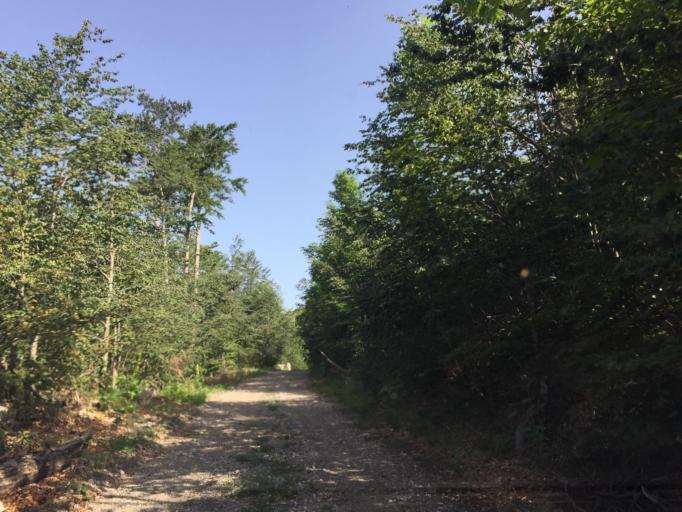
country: HR
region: Primorsko-Goranska
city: Krasica
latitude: 45.4155
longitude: 14.5912
